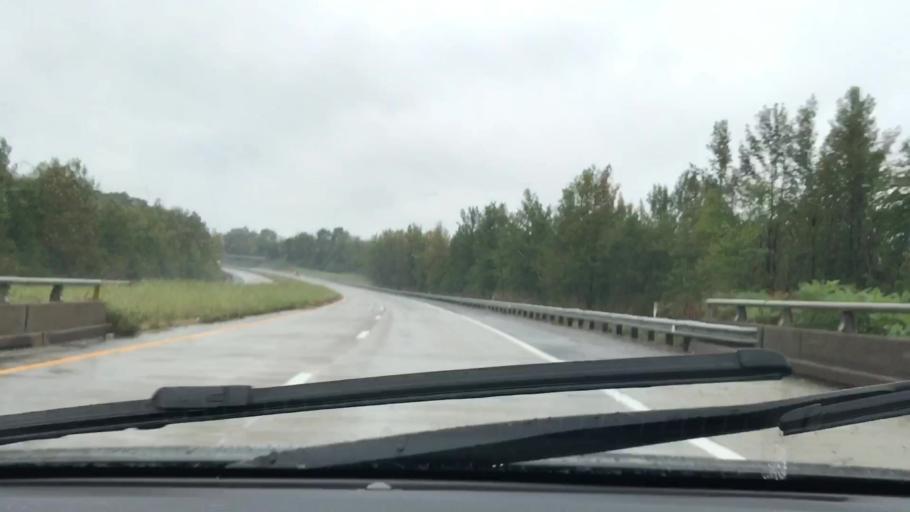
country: US
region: Kentucky
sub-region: Hopkins County
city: Nortonville
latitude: 37.1468
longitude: -87.4652
